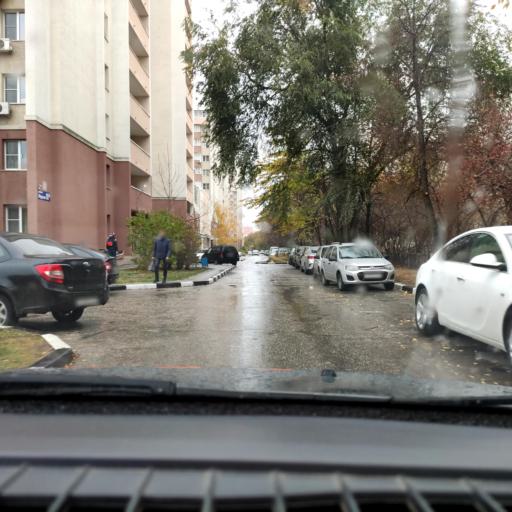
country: RU
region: Samara
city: Tol'yatti
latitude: 53.5144
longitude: 49.2910
